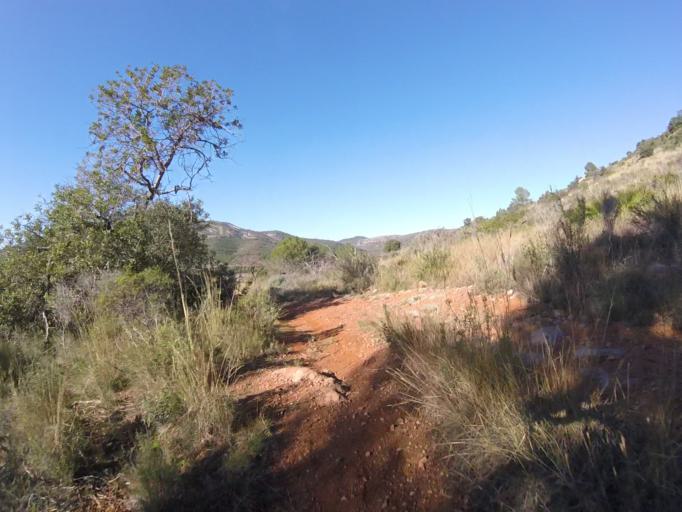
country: ES
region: Valencia
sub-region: Provincia de Castello
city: Orpesa/Oropesa del Mar
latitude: 40.1220
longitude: 0.1182
